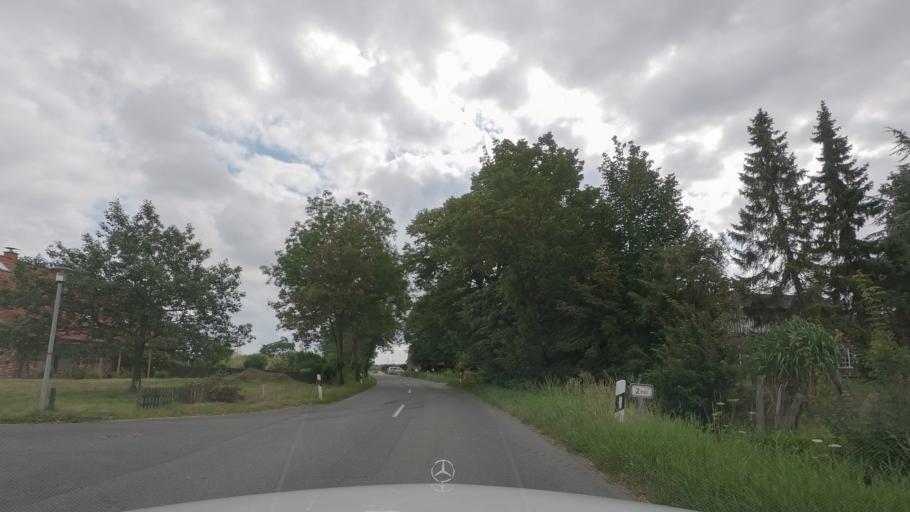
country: DE
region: Lower Saxony
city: Uthlede
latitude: 53.3086
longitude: 8.5345
